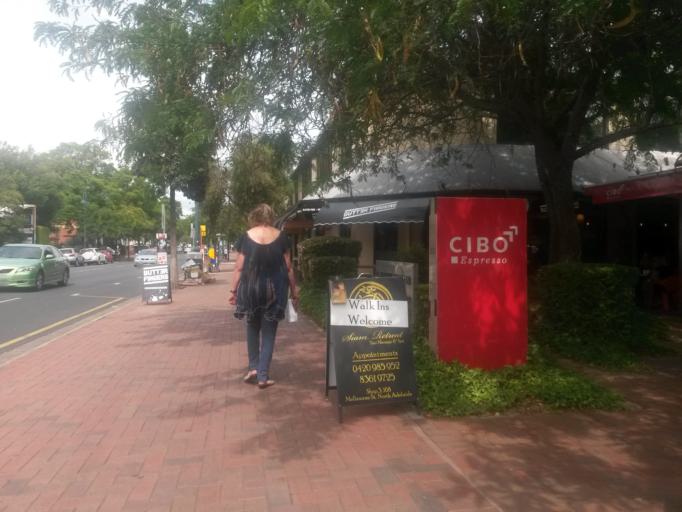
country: AU
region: South Australia
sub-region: Adelaide
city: North Adelaide
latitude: -34.9078
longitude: 138.6057
